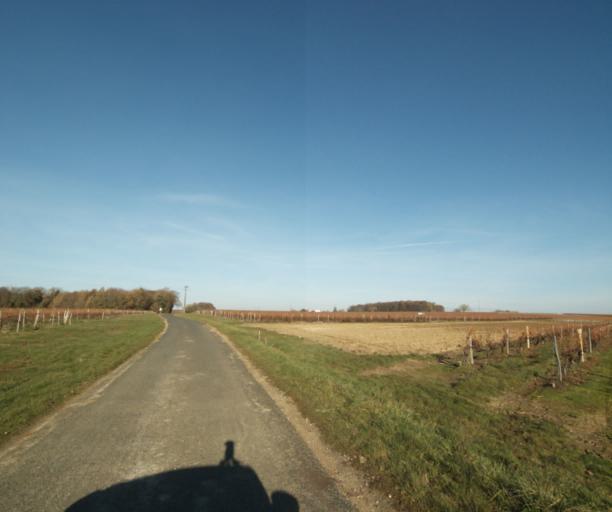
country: FR
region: Poitou-Charentes
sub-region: Departement de la Charente-Maritime
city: Cherac
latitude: 45.7290
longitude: -0.4479
